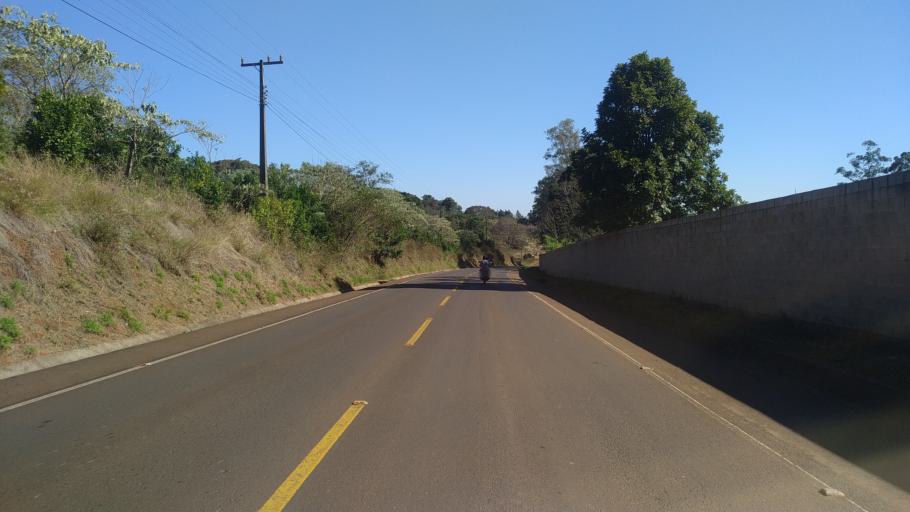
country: BR
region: Santa Catarina
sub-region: Chapeco
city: Chapeco
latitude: -27.1571
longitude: -52.6124
